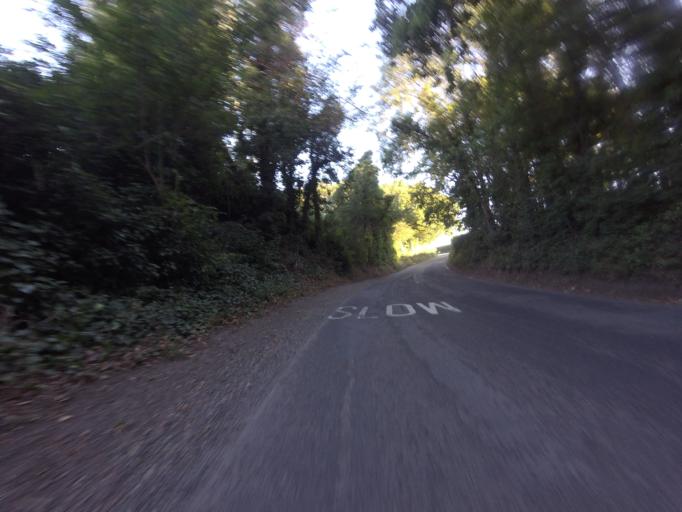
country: GB
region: England
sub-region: Kent
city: Sturry
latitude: 51.3262
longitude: 1.1944
